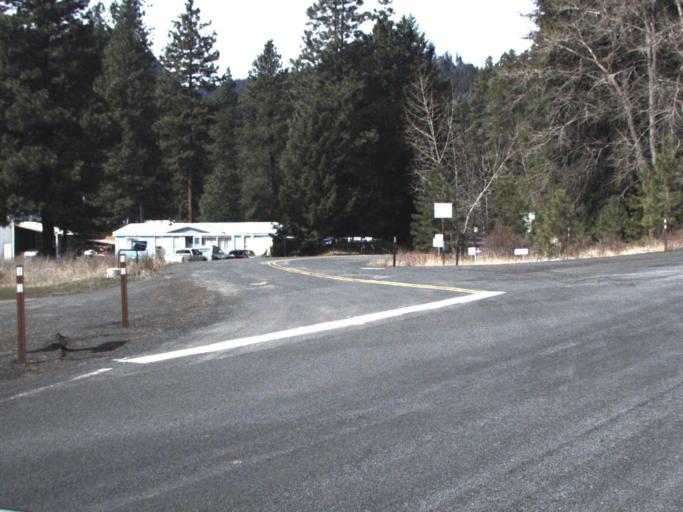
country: US
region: Washington
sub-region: Kittitas County
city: Cle Elum
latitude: 46.9181
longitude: -121.0431
